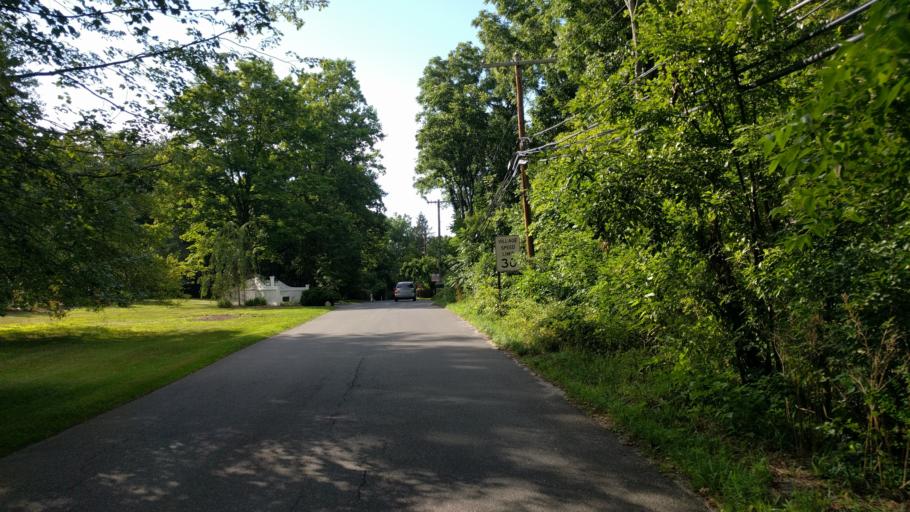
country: US
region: New York
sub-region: Nassau County
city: Oyster Bay Cove
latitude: 40.8706
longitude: -73.5028
